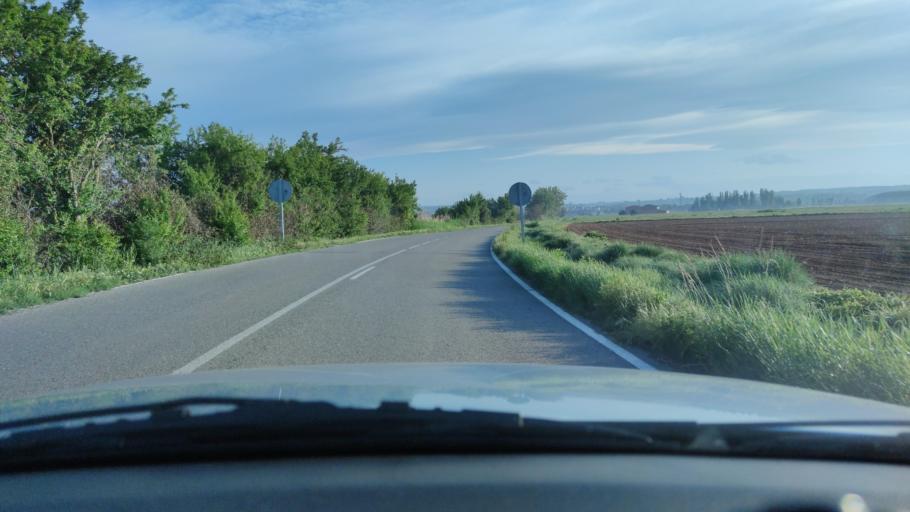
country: ES
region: Catalonia
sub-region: Provincia de Lleida
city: Penelles
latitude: 41.7323
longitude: 0.9830
